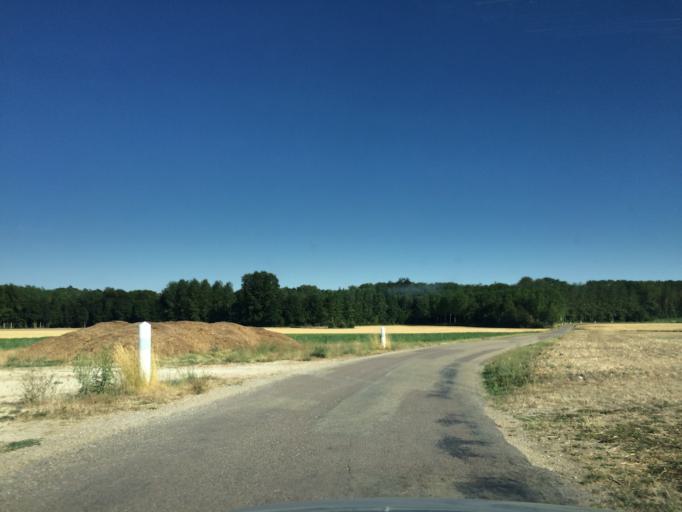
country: FR
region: Bourgogne
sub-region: Departement de l'Yonne
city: Fleury-la-Vallee
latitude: 47.9098
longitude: 3.4405
